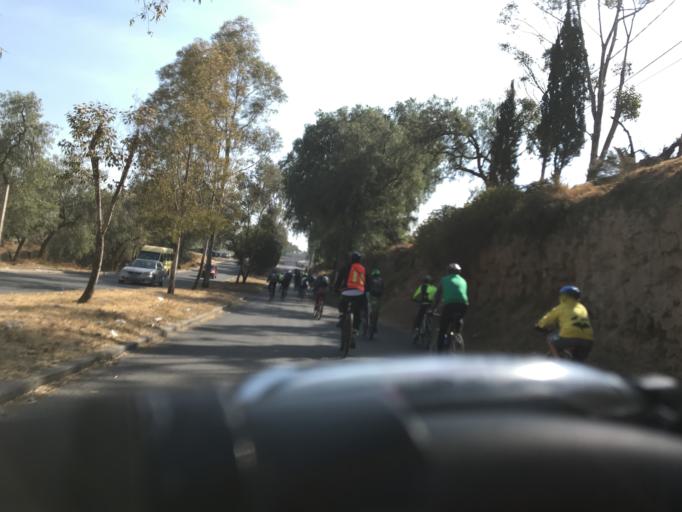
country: MX
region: Mexico
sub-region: Tecamac
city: Ojo de Agua
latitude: 19.6719
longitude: -99.0101
